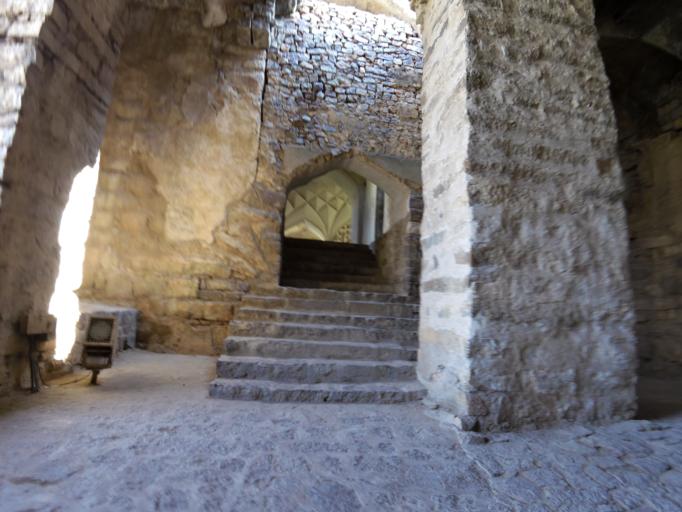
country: IN
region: Telangana
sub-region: Hyderabad
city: Hyderabad
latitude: 17.3837
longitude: 78.4019
